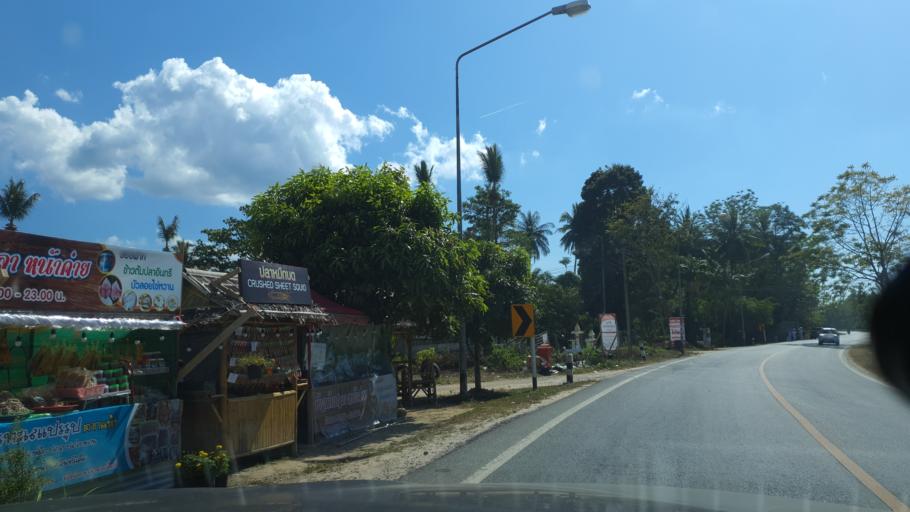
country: TH
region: Phangnga
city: Ban Khao Lak
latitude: 8.5871
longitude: 98.2492
